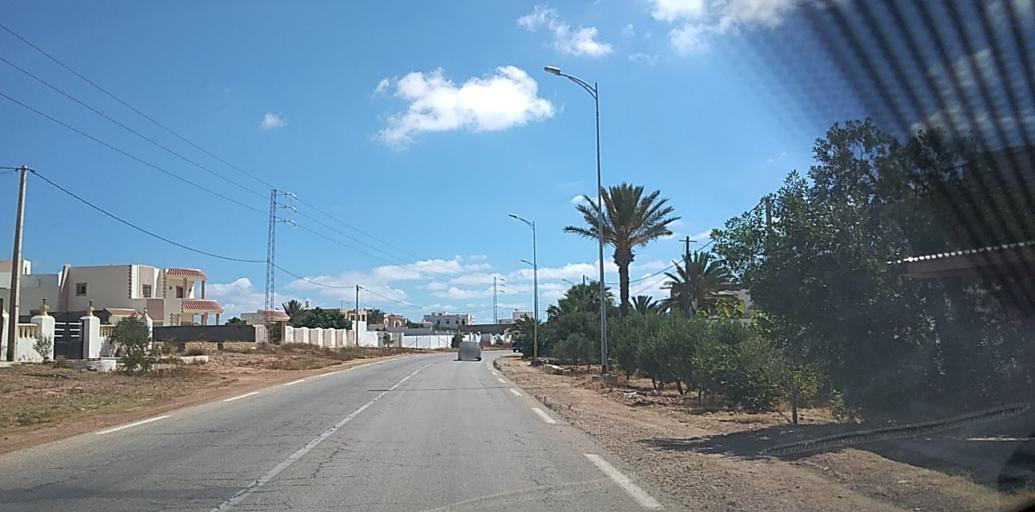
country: TN
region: Safaqis
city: Al Qarmadah
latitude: 34.6760
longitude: 11.1488
